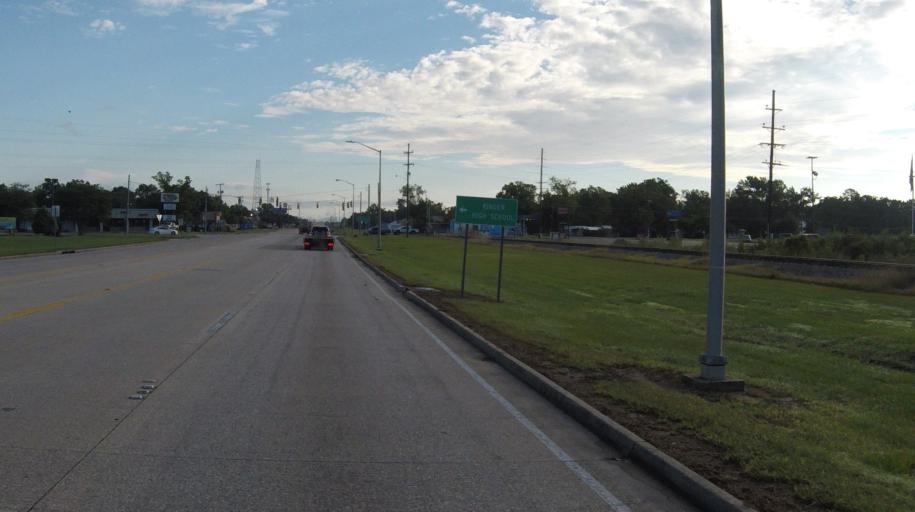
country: US
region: Louisiana
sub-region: Allen Parish
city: Kinder
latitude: 30.4809
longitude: -92.8523
